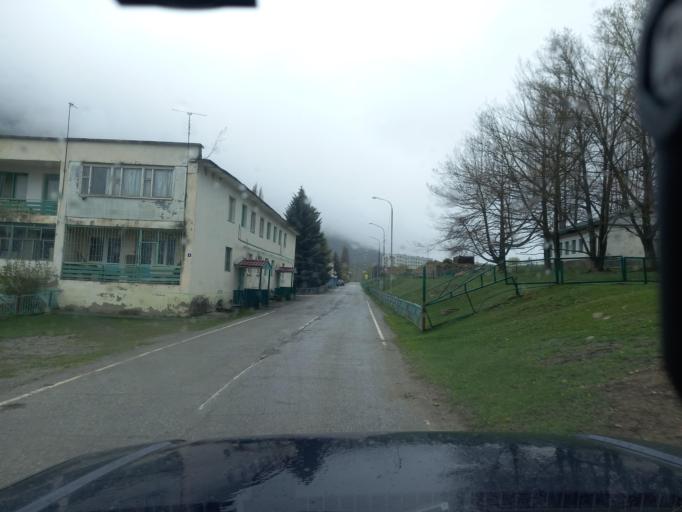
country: RU
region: Kabardino-Balkariya
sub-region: El'brusskiy Rayon
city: El'brus
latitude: 43.2790
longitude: 42.6899
